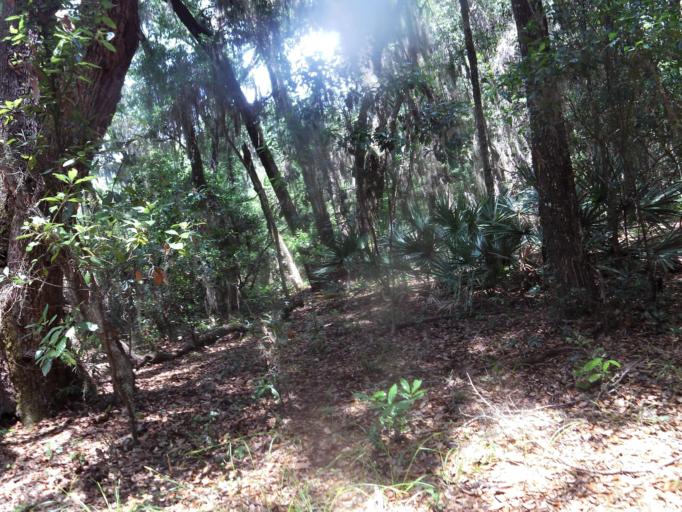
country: US
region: Florida
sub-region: Nassau County
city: Fernandina Beach
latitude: 30.4939
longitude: -81.4882
